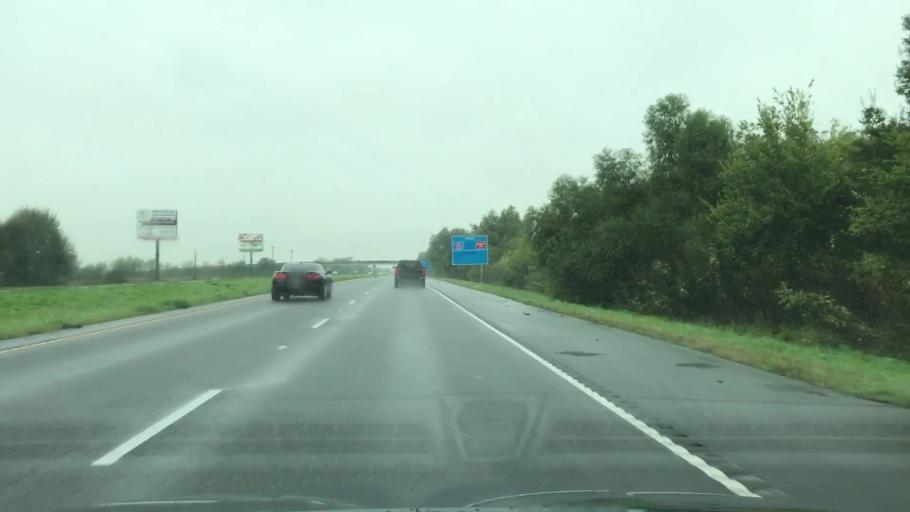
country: US
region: Louisiana
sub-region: Lafourche Parish
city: Raceland
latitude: 29.6899
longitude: -90.6174
